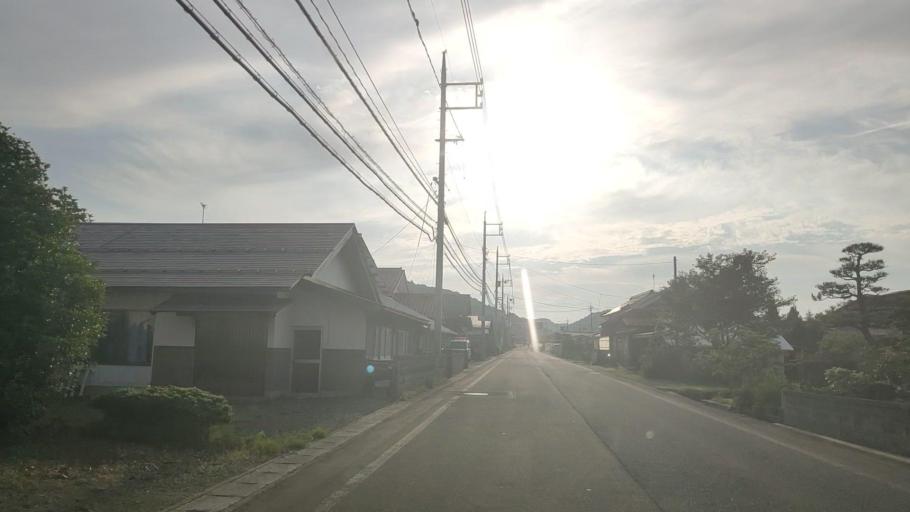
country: JP
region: Tottori
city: Kurayoshi
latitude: 35.2801
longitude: 133.6392
